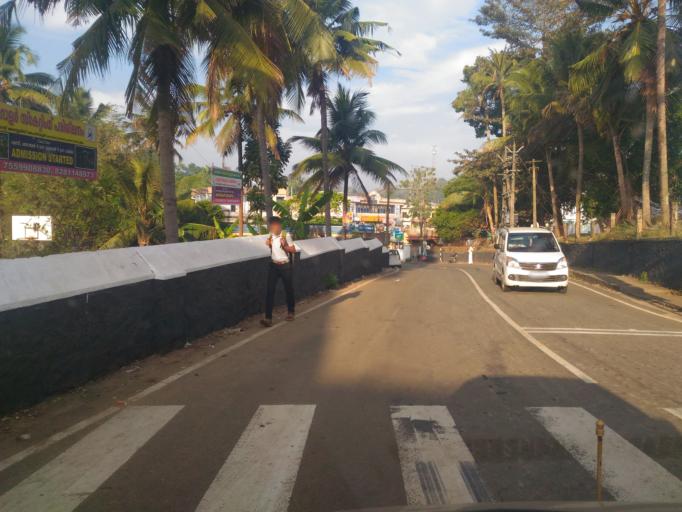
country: IN
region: Kerala
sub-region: Kottayam
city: Palackattumala
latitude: 9.7901
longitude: 76.6609
